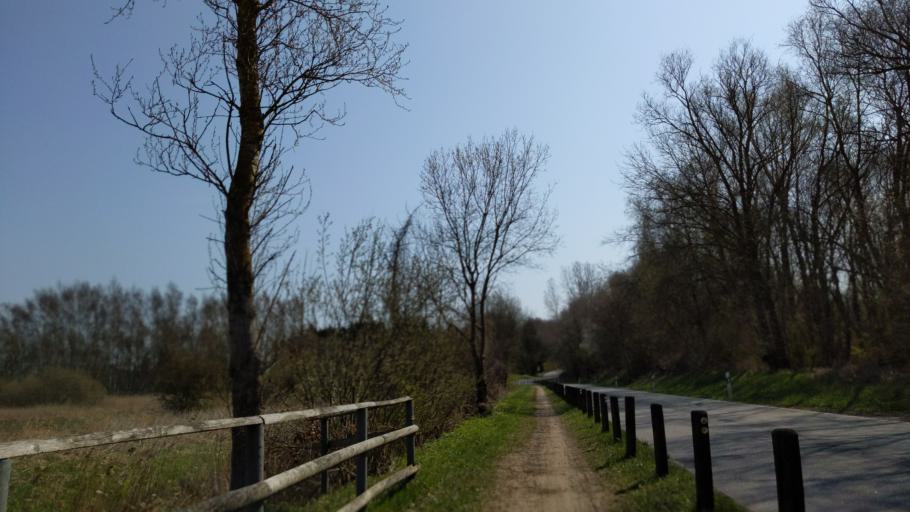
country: DE
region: Schleswig-Holstein
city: Travemuende
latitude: 53.9496
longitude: 10.9109
